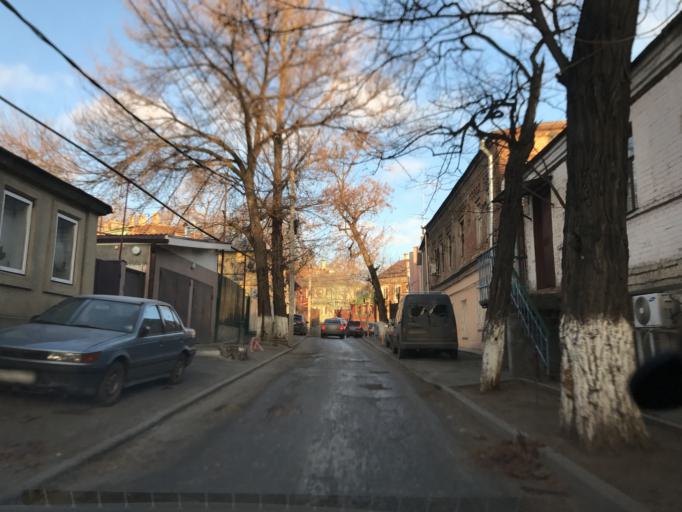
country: RU
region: Rostov
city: Rostov-na-Donu
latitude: 47.2189
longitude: 39.6842
